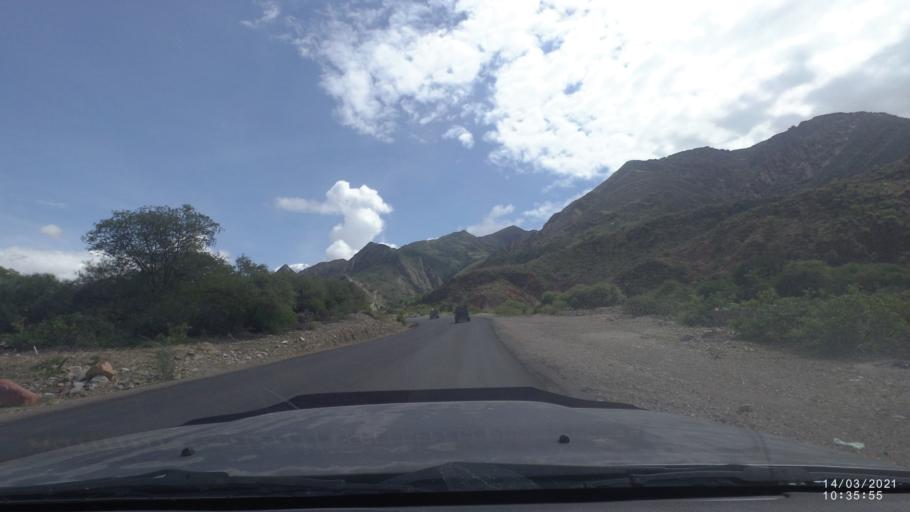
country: BO
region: Cochabamba
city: Cliza
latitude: -17.9055
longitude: -65.8809
